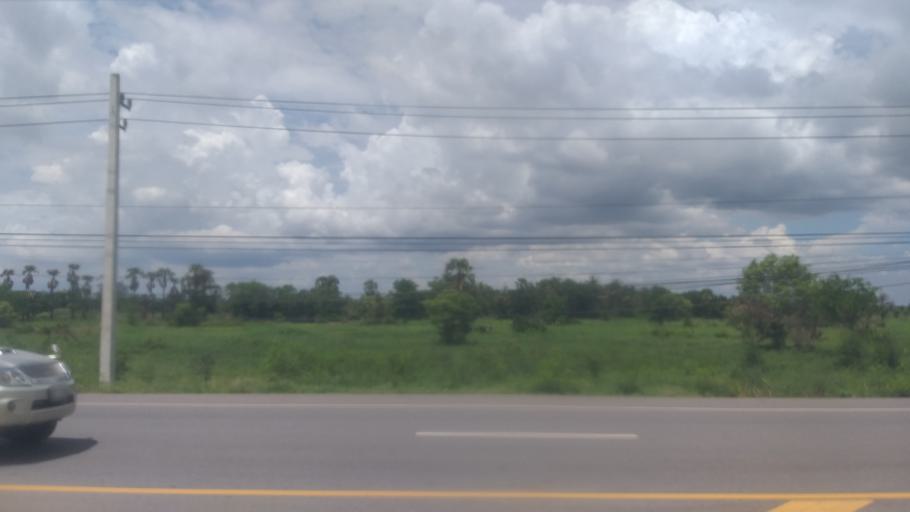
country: TH
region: Nakhon Ratchasima
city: Non Thai
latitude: 15.1306
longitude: 102.1039
